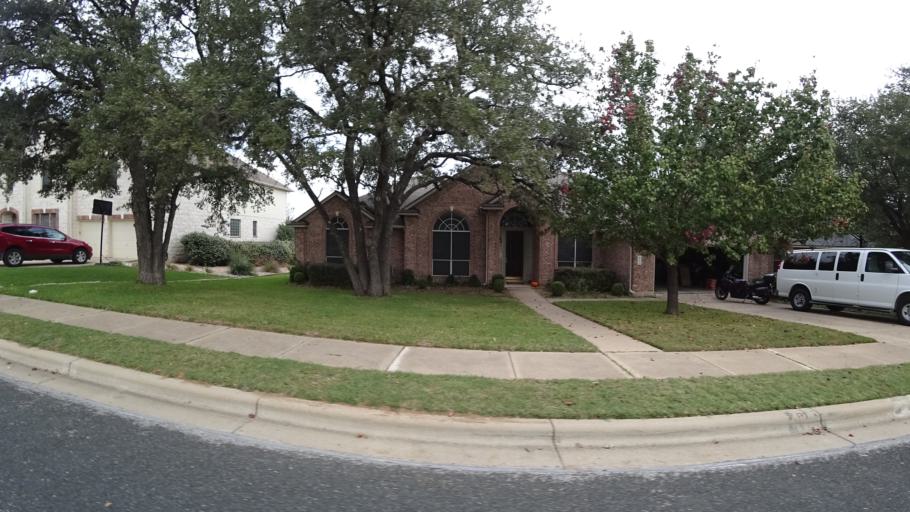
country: US
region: Texas
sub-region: Travis County
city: Shady Hollow
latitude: 30.1563
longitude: -97.8481
